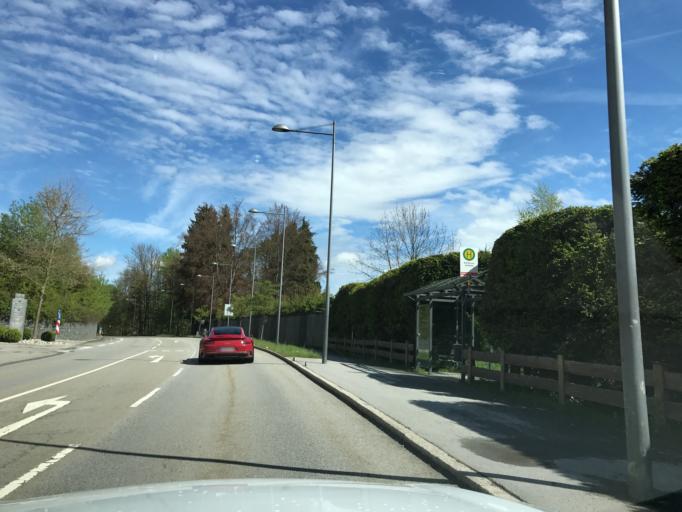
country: DE
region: Bavaria
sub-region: Upper Bavaria
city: Bad Wiessee
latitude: 47.7259
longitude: 11.7180
